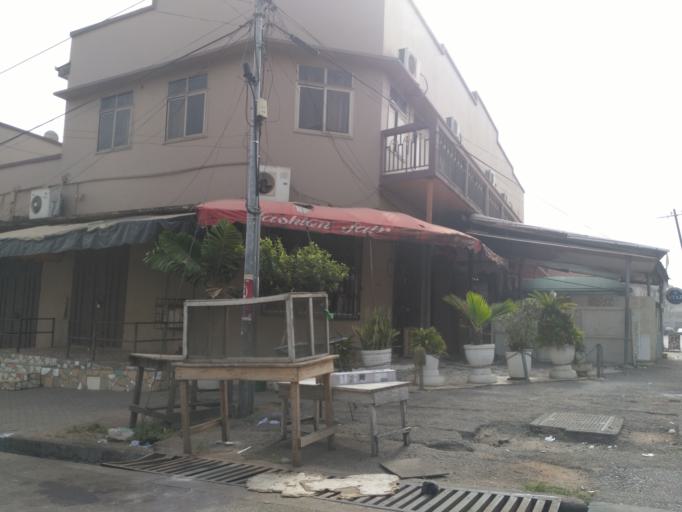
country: GH
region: Ashanti
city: Kumasi
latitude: 6.6913
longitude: -1.6212
